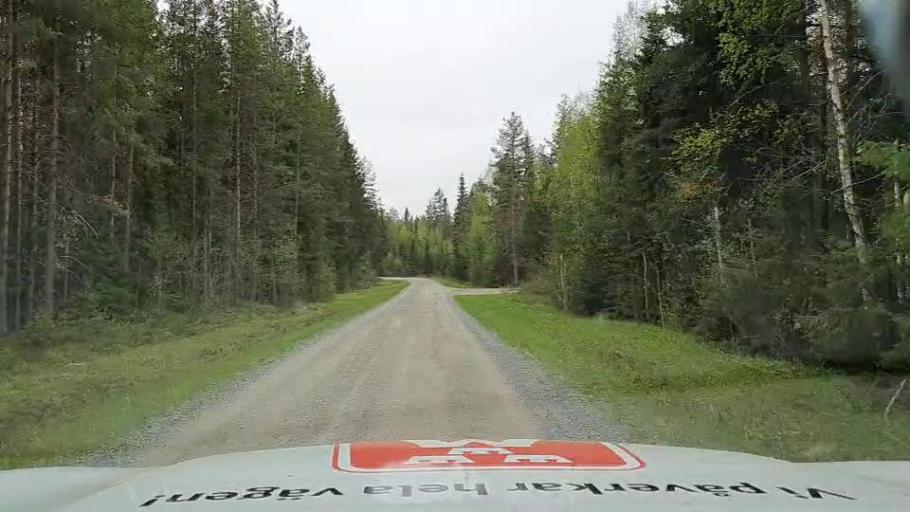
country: SE
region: Jaemtland
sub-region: Bergs Kommun
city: Hoverberg
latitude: 62.5086
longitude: 14.7010
